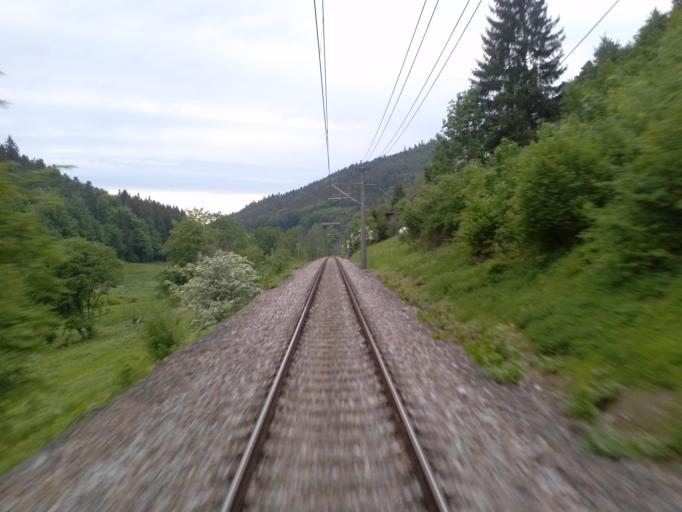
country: DE
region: Baden-Wuerttemberg
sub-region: Karlsruhe Region
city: Bad Herrenalb
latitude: 48.8139
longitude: 8.4442
